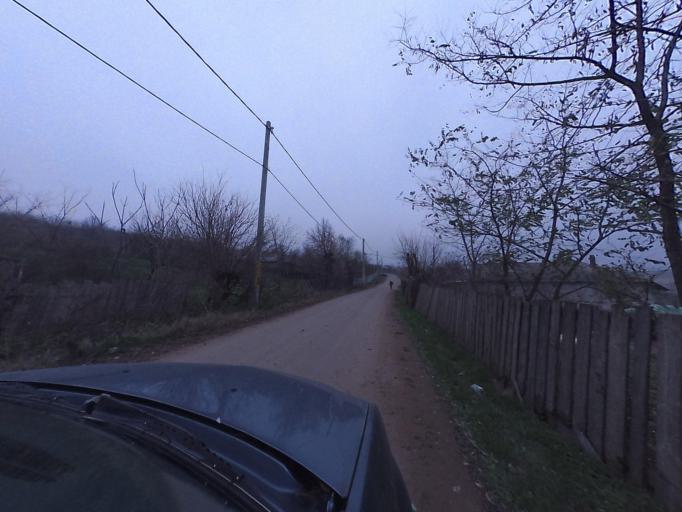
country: RO
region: Vaslui
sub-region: Comuna Vinderei
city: Vinderei
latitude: 46.1370
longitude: 27.7520
